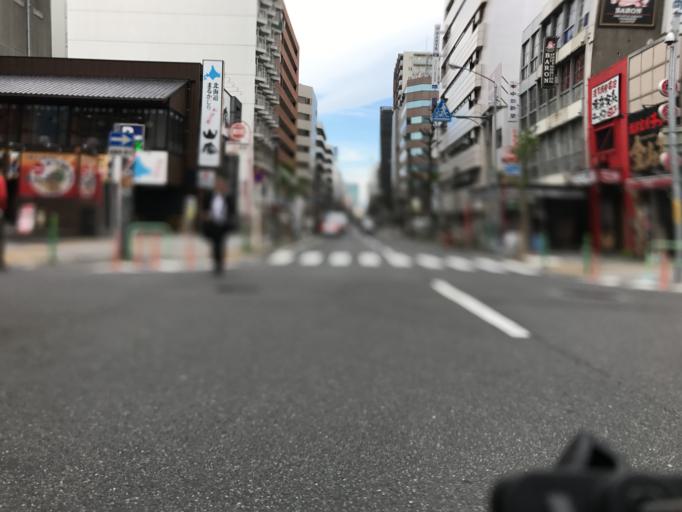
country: JP
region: Aichi
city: Nagoya-shi
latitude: 35.1667
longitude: 136.9037
